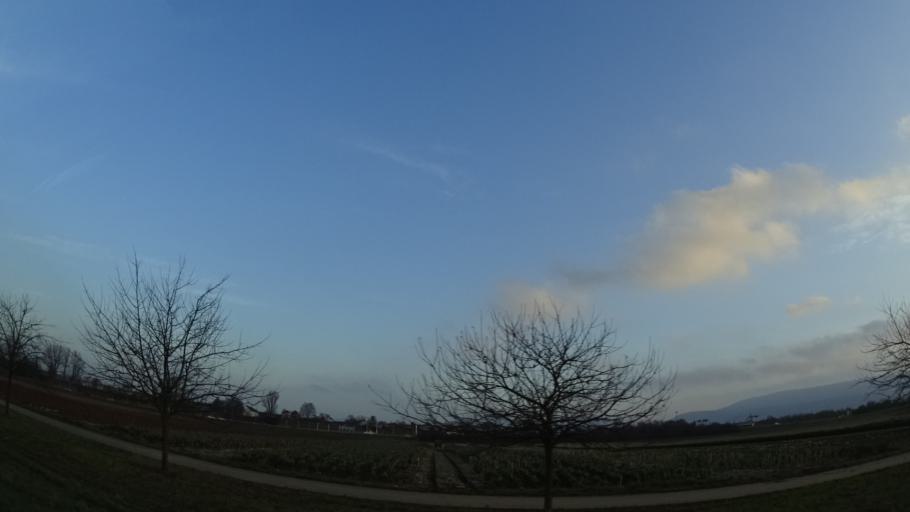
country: DE
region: Baden-Wuerttemberg
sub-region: Karlsruhe Region
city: Eppelheim
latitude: 49.3678
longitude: 8.6256
